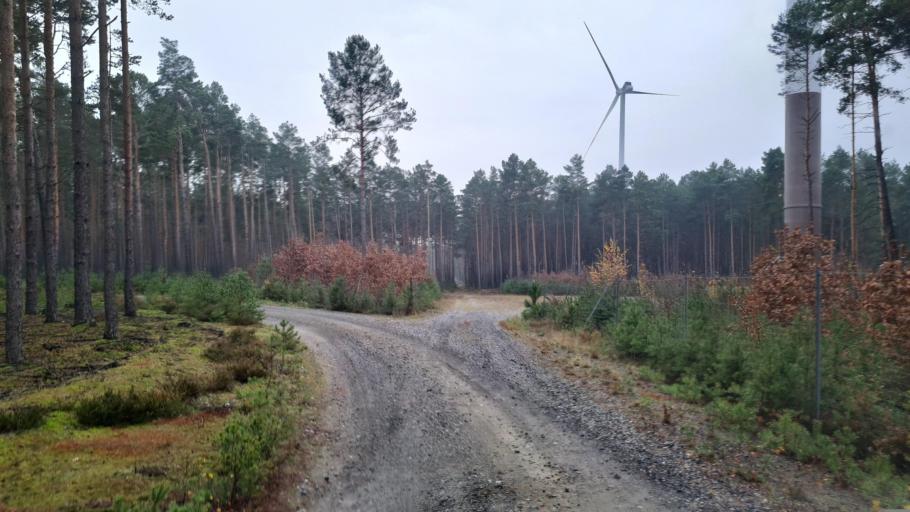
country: DE
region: Brandenburg
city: Sallgast
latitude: 51.6411
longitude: 13.8093
